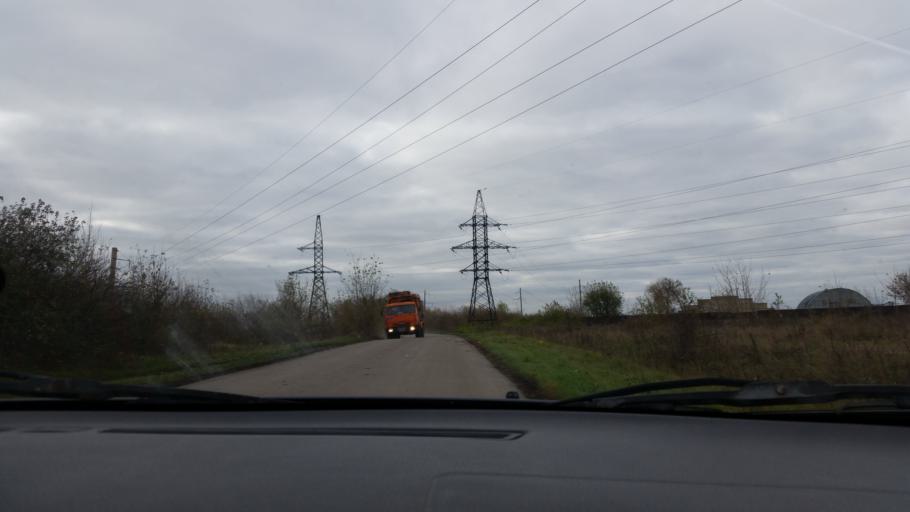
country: RU
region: Lipetsk
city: Gryazi
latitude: 52.4669
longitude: 39.9386
